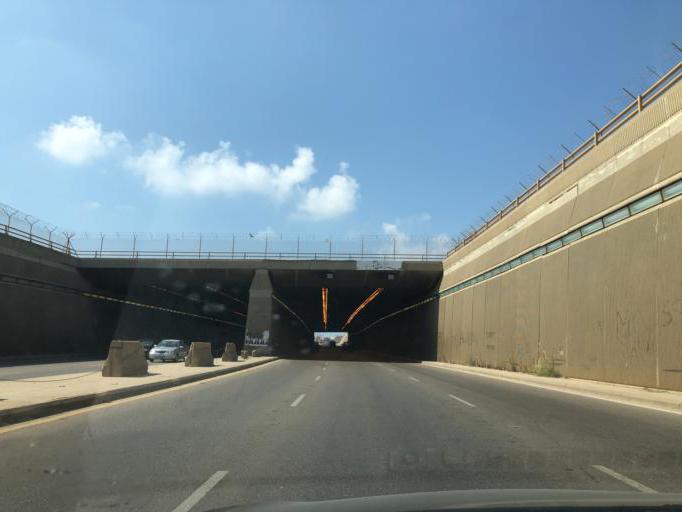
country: LB
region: Mont-Liban
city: Baabda
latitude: 33.8212
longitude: 35.4864
